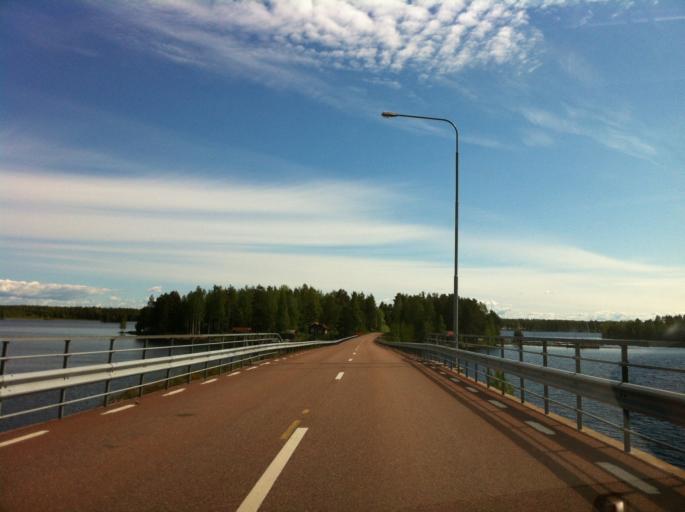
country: SE
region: Dalarna
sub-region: Mora Kommun
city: Mora
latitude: 60.8952
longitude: 14.5595
